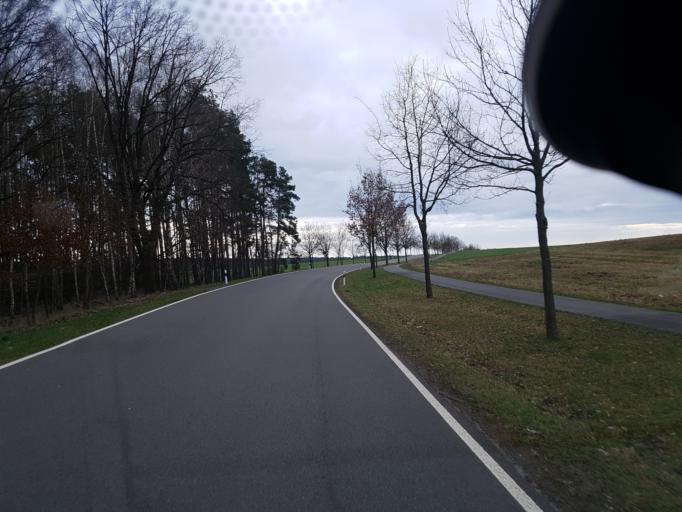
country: DE
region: Brandenburg
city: Gross Lindow
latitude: 52.1571
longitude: 14.5157
